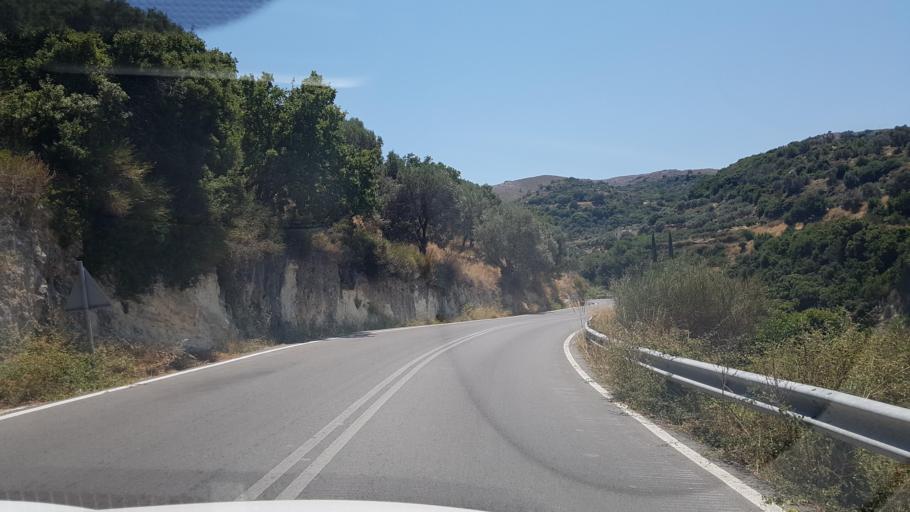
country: GR
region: Crete
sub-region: Nomos Rethymnis
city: Agia Foteini
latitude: 35.3363
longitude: 24.6104
